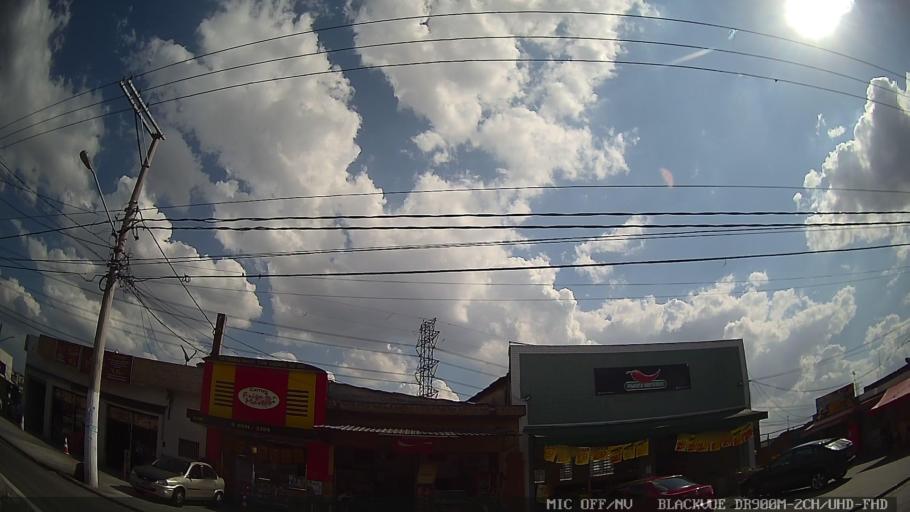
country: BR
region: Sao Paulo
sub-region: Ferraz De Vasconcelos
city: Ferraz de Vasconcelos
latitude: -23.5134
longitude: -46.4262
